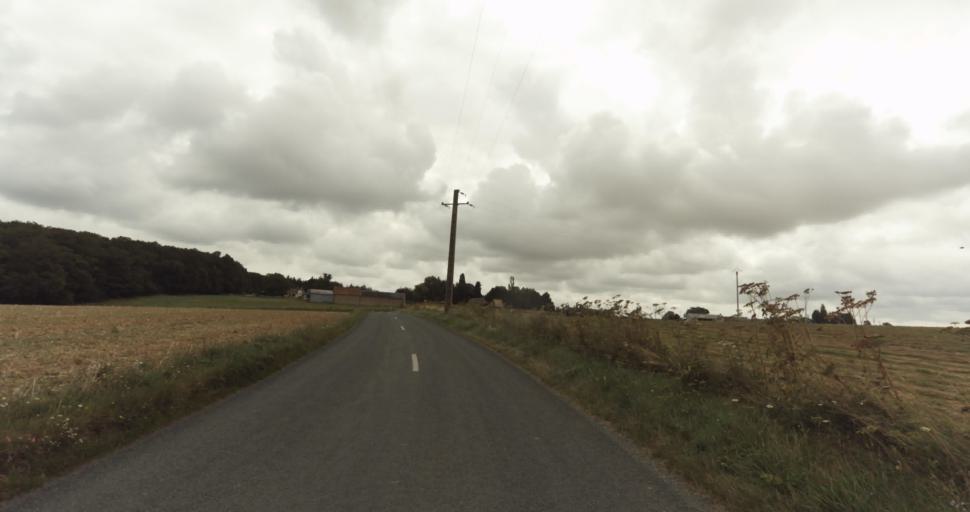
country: FR
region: Haute-Normandie
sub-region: Departement de l'Eure
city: La Couture-Boussey
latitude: 48.9471
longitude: 1.3601
